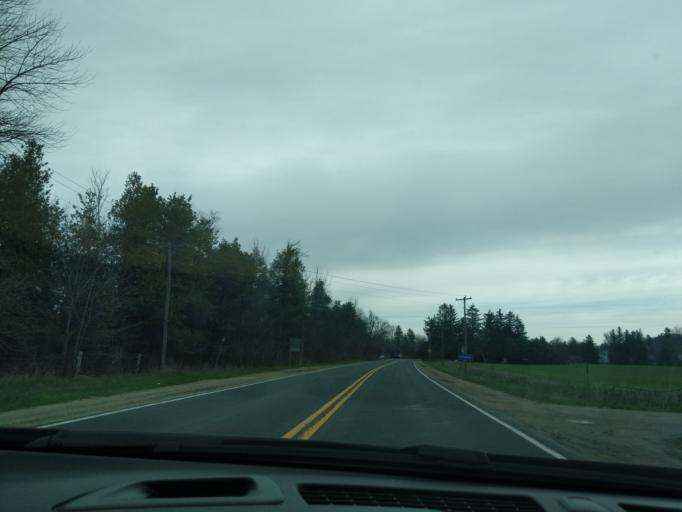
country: CA
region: Ontario
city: Orangeville
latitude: 44.0200
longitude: -79.9734
